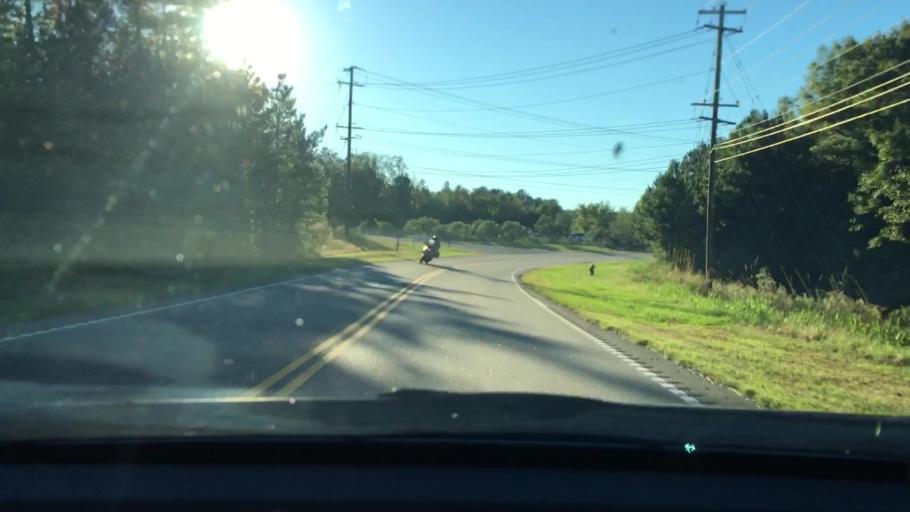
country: US
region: South Carolina
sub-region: Lexington County
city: Irmo
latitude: 34.1025
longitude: -81.1768
